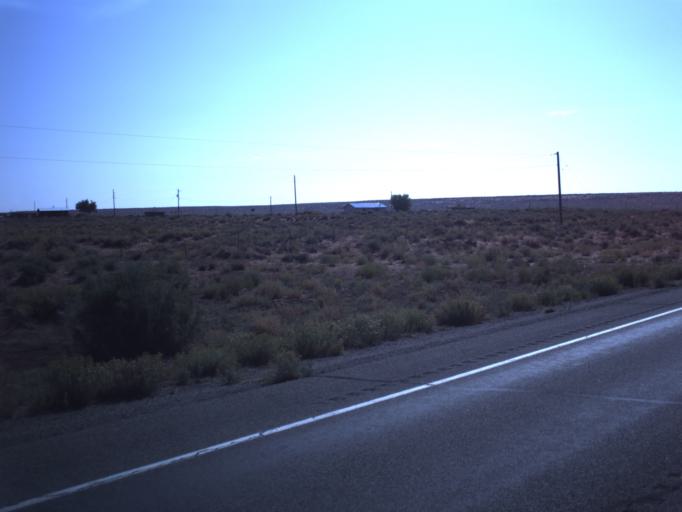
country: US
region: Utah
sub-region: San Juan County
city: Blanding
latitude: 37.1740
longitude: -109.5828
